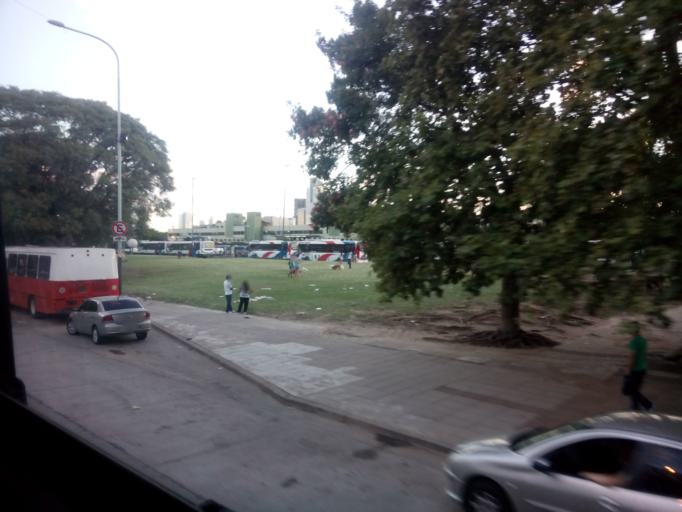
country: AR
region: Buenos Aires F.D.
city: Retiro
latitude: -34.5849
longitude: -58.3739
